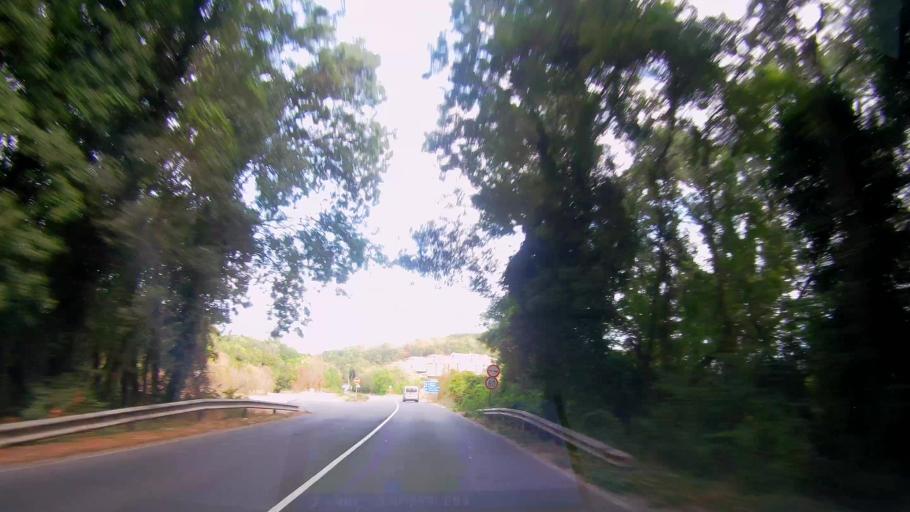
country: BG
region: Burgas
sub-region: Obshtina Primorsko
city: Primorsko
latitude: 42.3311
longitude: 27.7286
